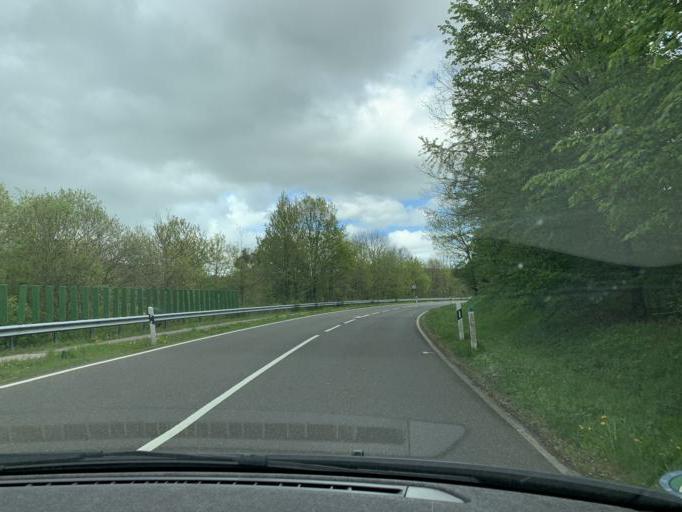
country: DE
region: North Rhine-Westphalia
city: Heimbach
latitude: 50.6510
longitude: 6.4787
